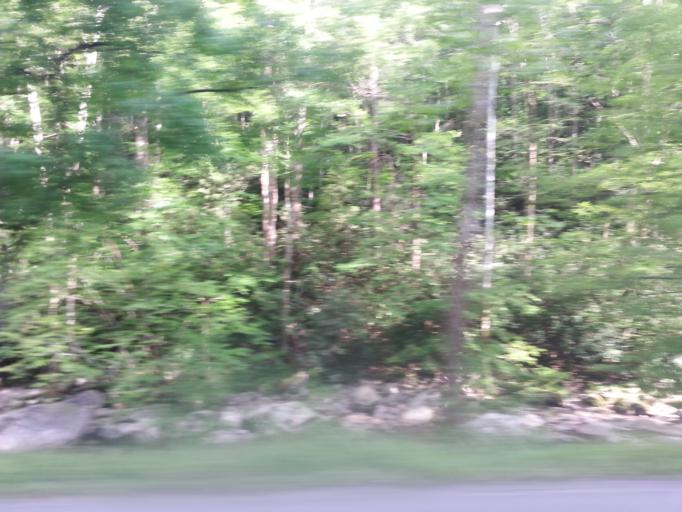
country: US
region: Tennessee
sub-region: Sevier County
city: Gatlinburg
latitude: 35.6691
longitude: -83.6683
